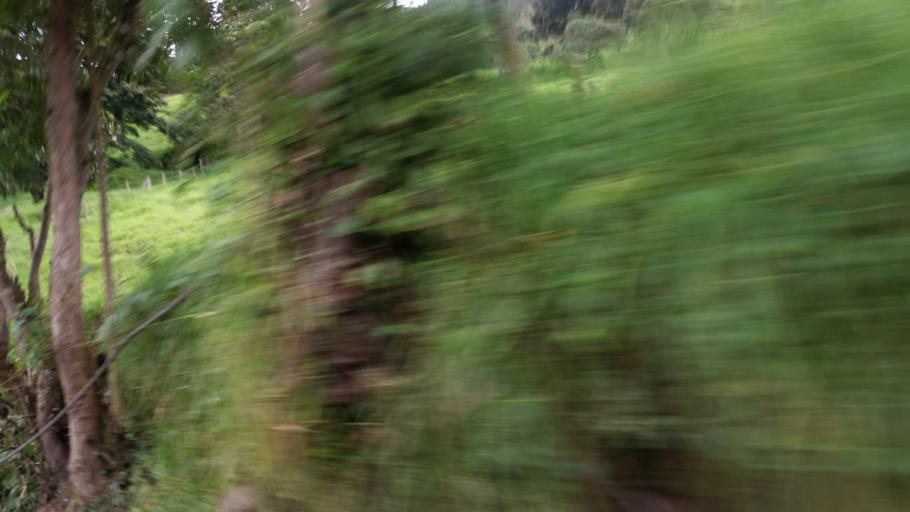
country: CO
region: Cundinamarca
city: Choachi
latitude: 4.5621
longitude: -73.9486
